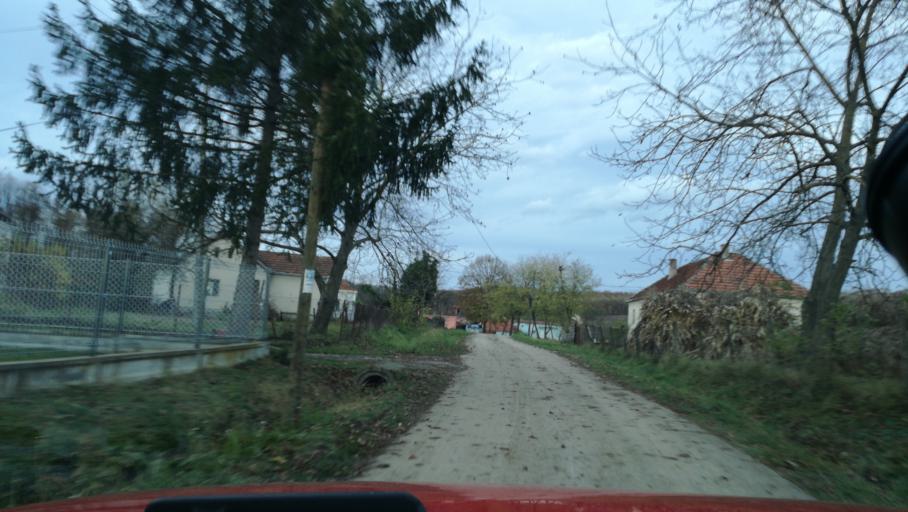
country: RS
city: Prislonica
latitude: 43.9060
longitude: 20.4366
